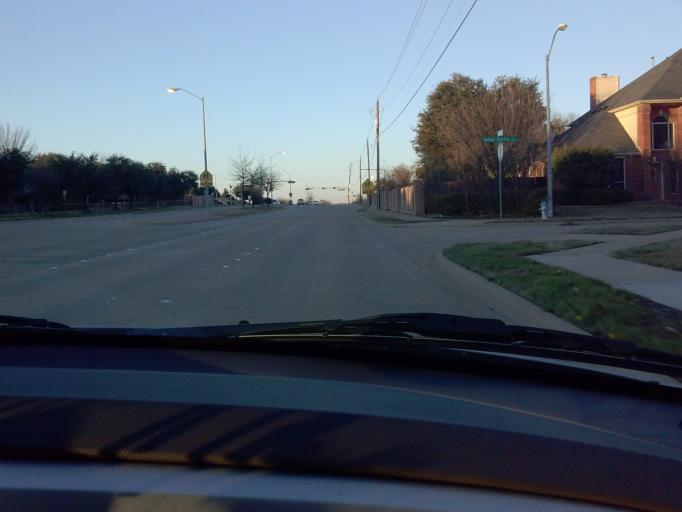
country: US
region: Texas
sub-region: Collin County
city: Allen
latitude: 33.0844
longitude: -96.7499
